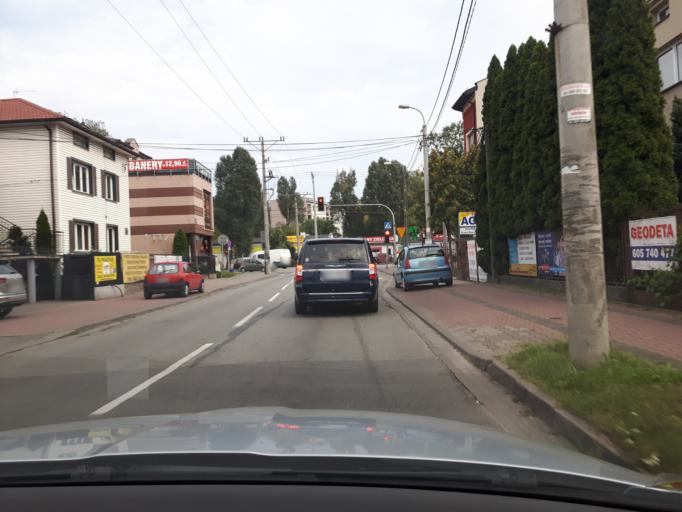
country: PL
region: Masovian Voivodeship
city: Zielonka
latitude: 52.3039
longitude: 21.1601
